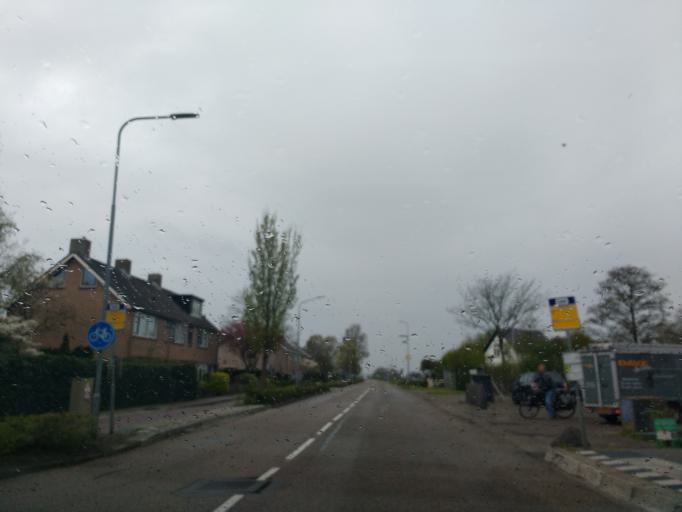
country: NL
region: North Holland
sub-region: Gemeente Schagen
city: Harenkarspel
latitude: 52.7224
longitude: 4.7339
